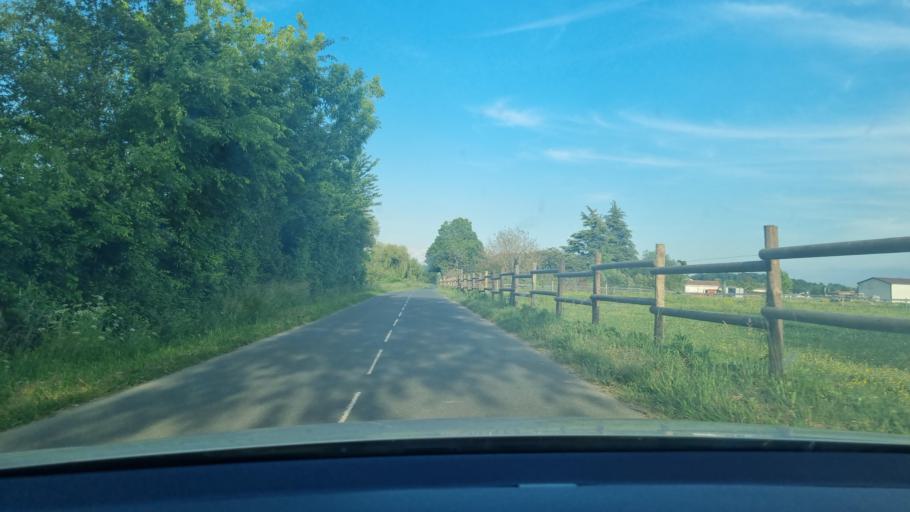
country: FR
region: Aquitaine
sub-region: Departement des Landes
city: Peyrehorade
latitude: 43.5453
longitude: -1.1748
